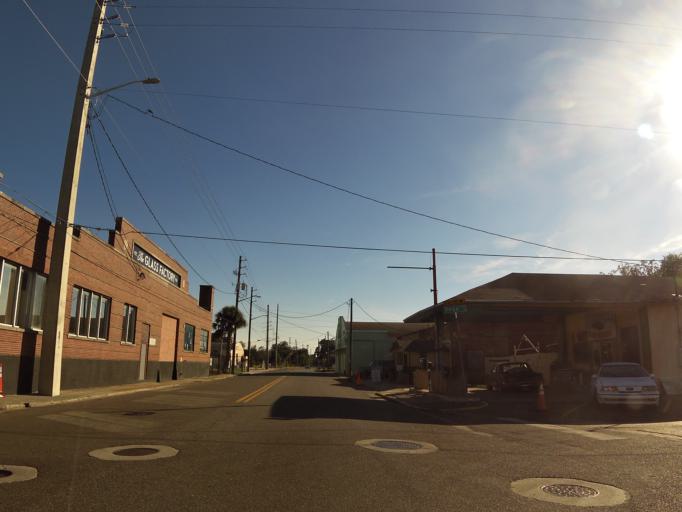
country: US
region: Florida
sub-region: Duval County
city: Jacksonville
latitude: 30.3353
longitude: -81.6760
